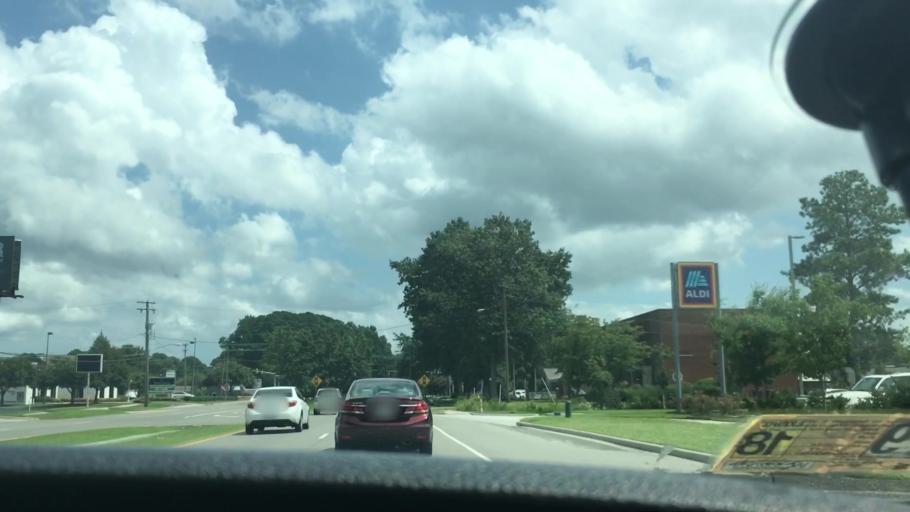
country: US
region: Virginia
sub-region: City of Portsmouth
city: Portsmouth Heights
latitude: 36.8606
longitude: -76.3943
